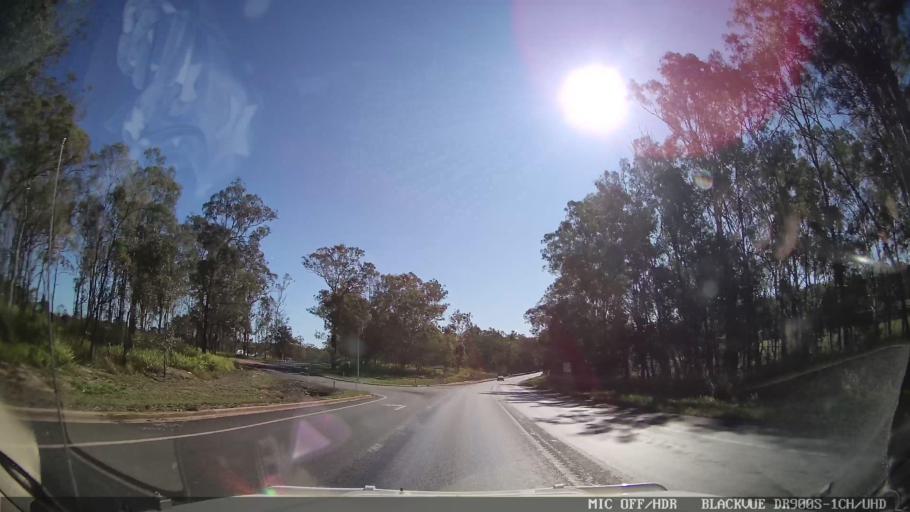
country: AU
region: Queensland
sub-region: Bundaberg
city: Childers
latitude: -25.2327
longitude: 152.2438
